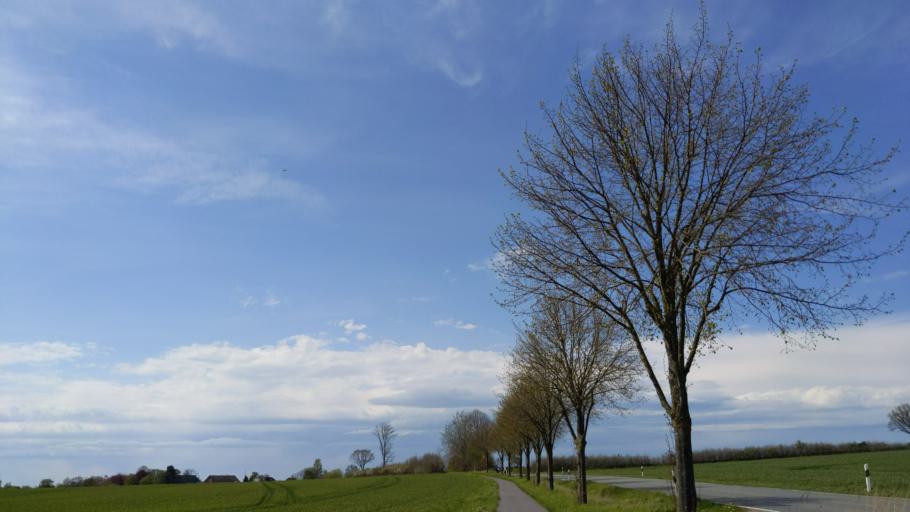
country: DE
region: Schleswig-Holstein
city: Stockelsdorf
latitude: 53.9269
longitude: 10.6473
